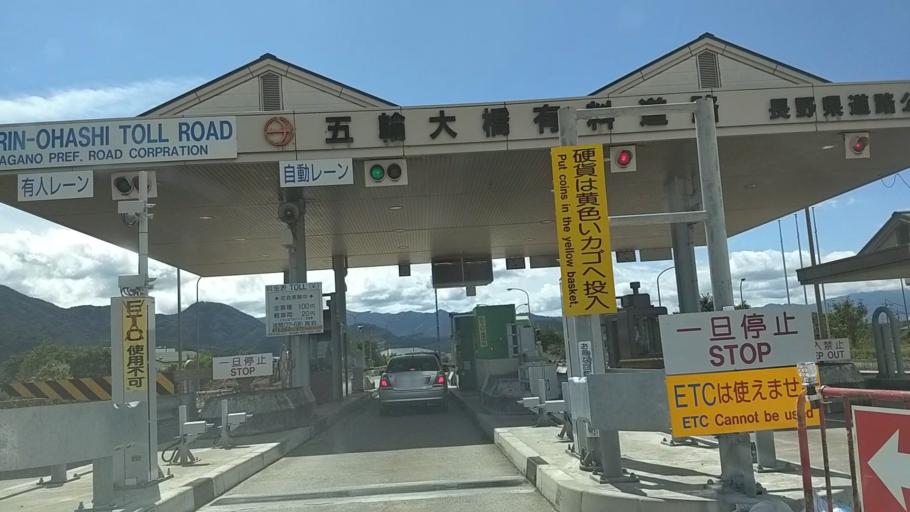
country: JP
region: Nagano
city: Nagano-shi
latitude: 36.6147
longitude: 138.2227
